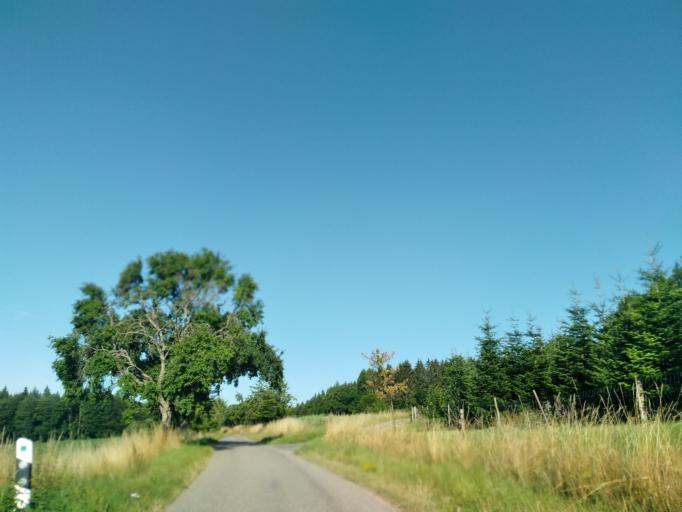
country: DE
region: Baden-Wuerttemberg
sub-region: Karlsruhe Region
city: Mudau
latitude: 49.5187
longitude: 9.1931
